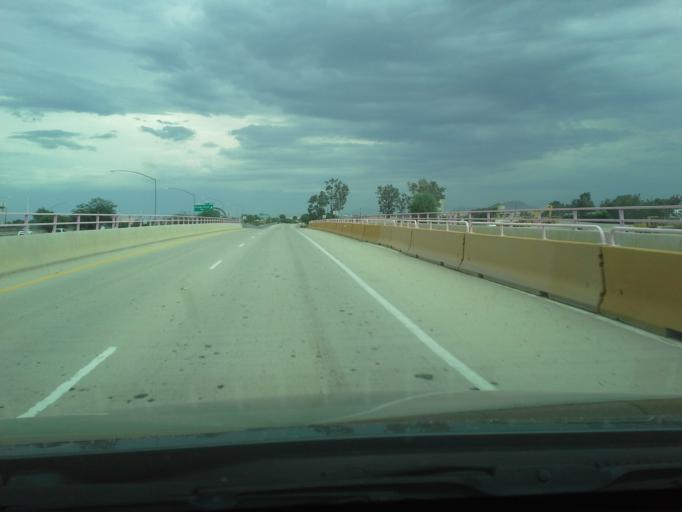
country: US
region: Arizona
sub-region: Pima County
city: Flowing Wells
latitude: 32.3287
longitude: -111.0575
